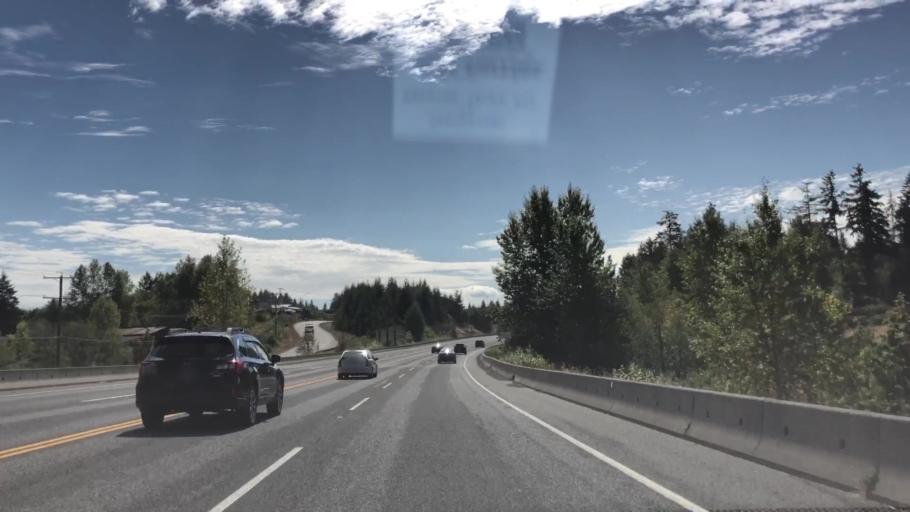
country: CA
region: British Columbia
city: Nanaimo
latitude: 49.1291
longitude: -123.8647
